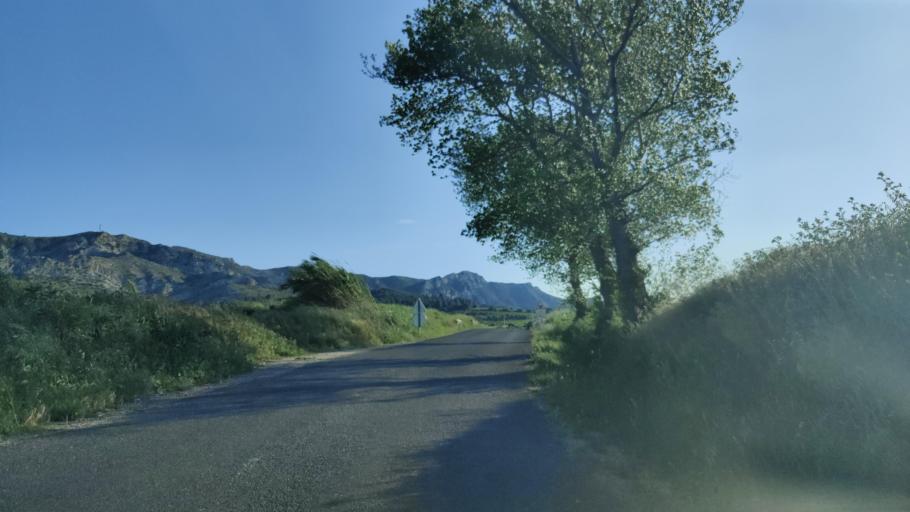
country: FR
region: Languedoc-Roussillon
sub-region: Departement des Pyrenees-Orientales
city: Baixas
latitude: 42.7811
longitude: 2.7795
